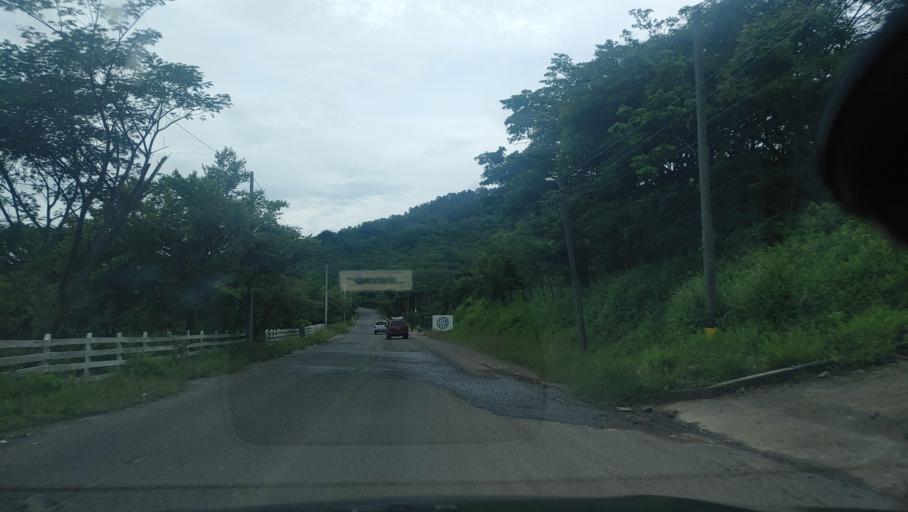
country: HN
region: Choluteca
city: San Marcos de Colon
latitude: 13.3805
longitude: -86.8708
